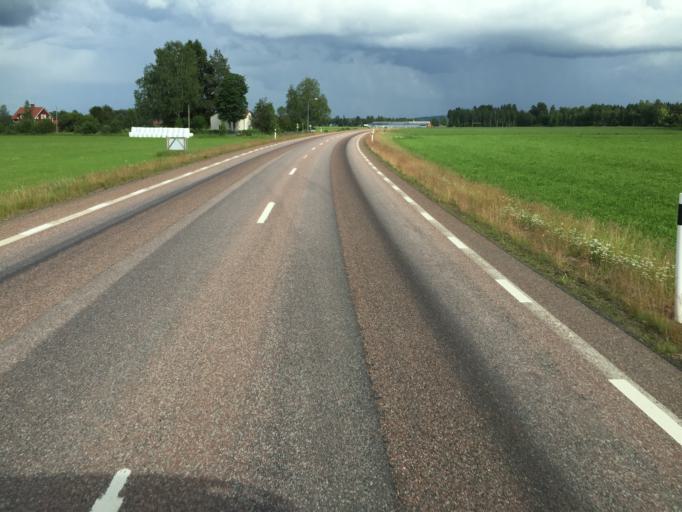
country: SE
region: Dalarna
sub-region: Vansbro Kommun
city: Jarna
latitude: 60.5545
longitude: 14.3378
